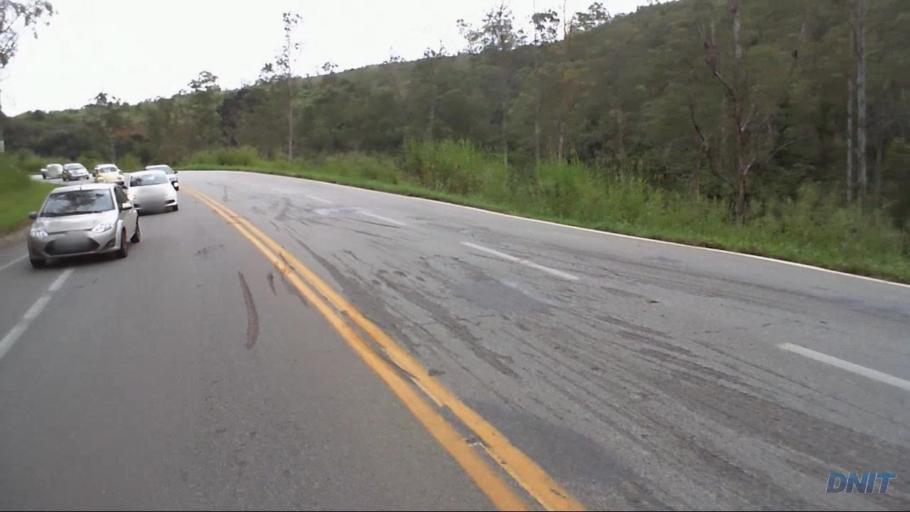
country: BR
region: Minas Gerais
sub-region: Nova Era
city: Nova Era
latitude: -19.8238
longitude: -43.0785
